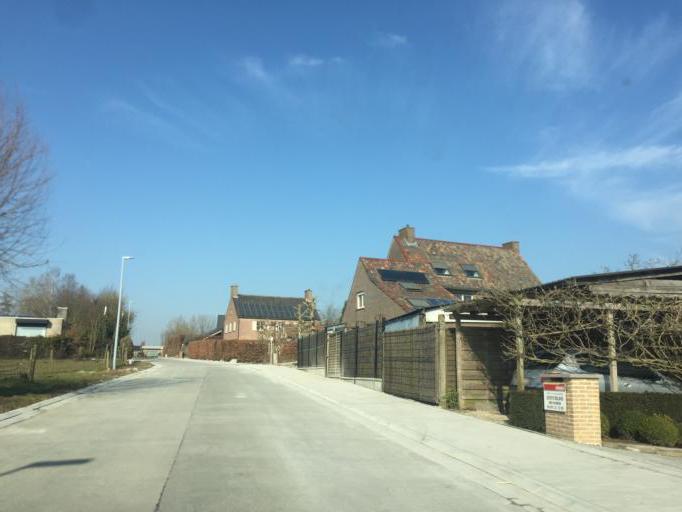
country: BE
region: Flanders
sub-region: Provincie West-Vlaanderen
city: Roeselare
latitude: 50.9266
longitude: 3.1292
